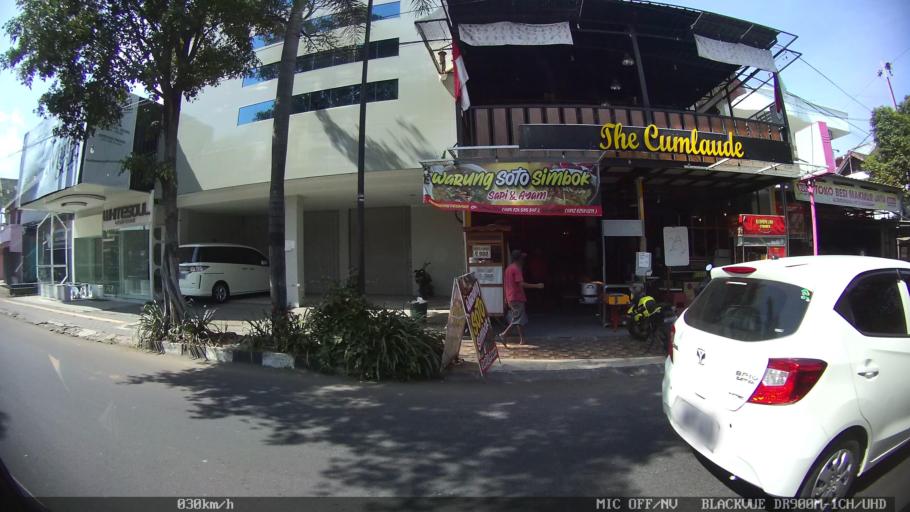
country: ID
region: Daerah Istimewa Yogyakarta
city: Yogyakarta
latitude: -7.8255
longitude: 110.3757
